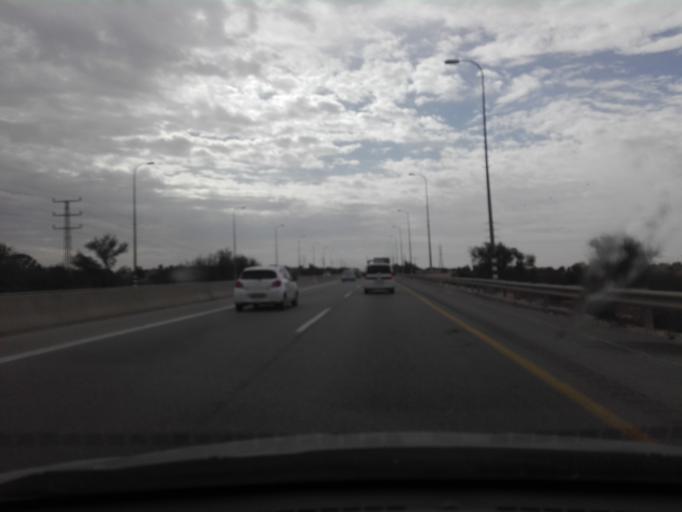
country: IL
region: Southern District
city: Lehavim
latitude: 31.3386
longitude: 34.7887
